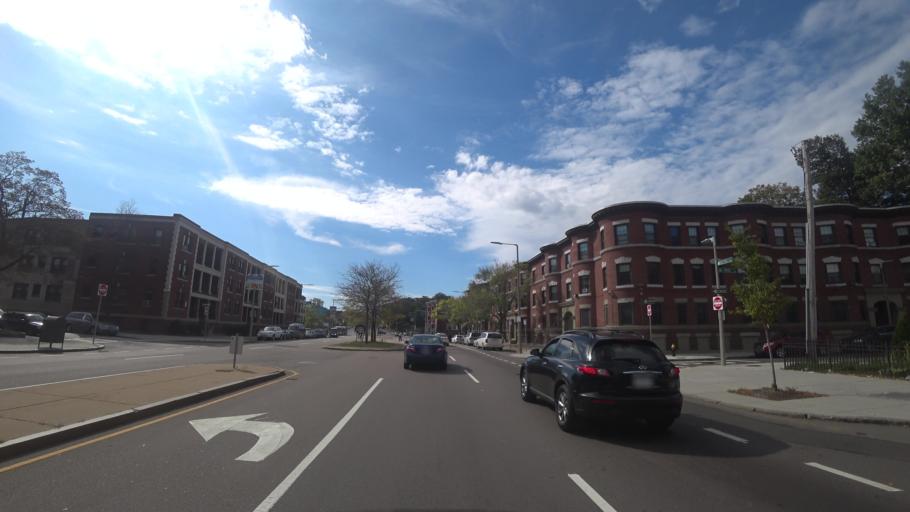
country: US
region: Massachusetts
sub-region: Suffolk County
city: Jamaica Plain
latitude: 42.3074
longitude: -71.0840
